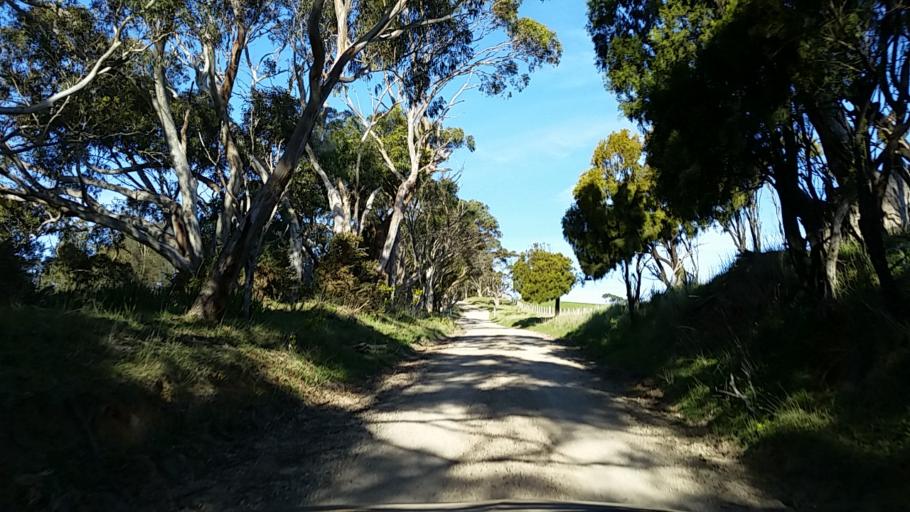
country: AU
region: South Australia
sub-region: Mount Barker
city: Meadows
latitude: -35.1915
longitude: 138.7796
